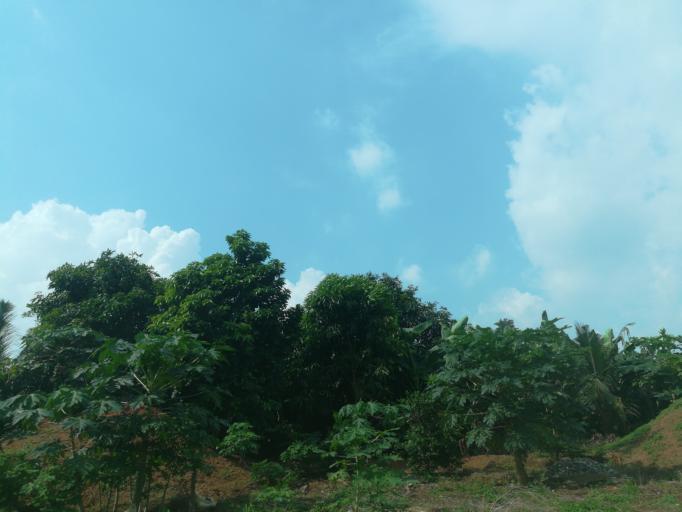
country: NG
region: Lagos
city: Ikorodu
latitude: 6.6402
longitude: 3.6691
